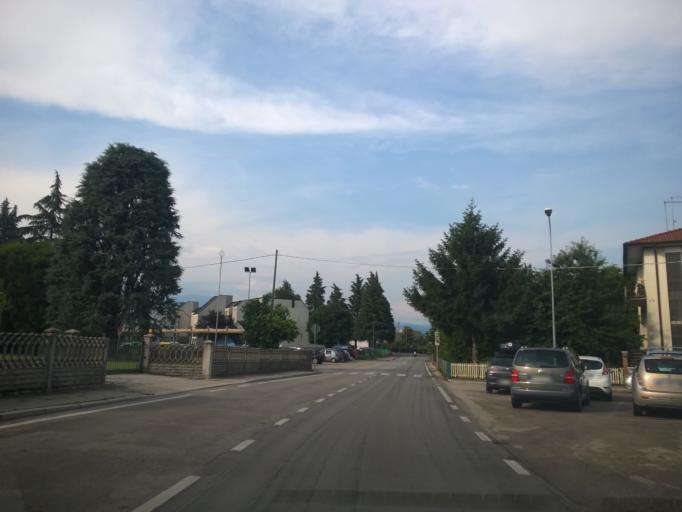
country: IT
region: Veneto
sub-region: Provincia di Vicenza
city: Malo
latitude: 45.6611
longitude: 11.4076
